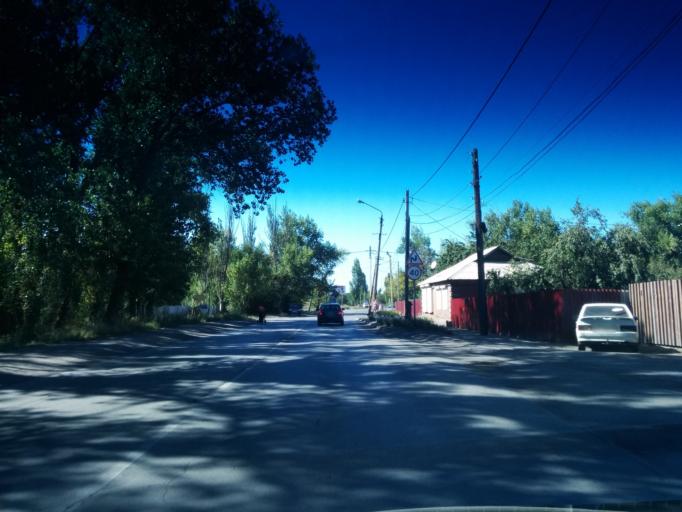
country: RU
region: Rostov
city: Shakhty
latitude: 47.6821
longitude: 40.2776
